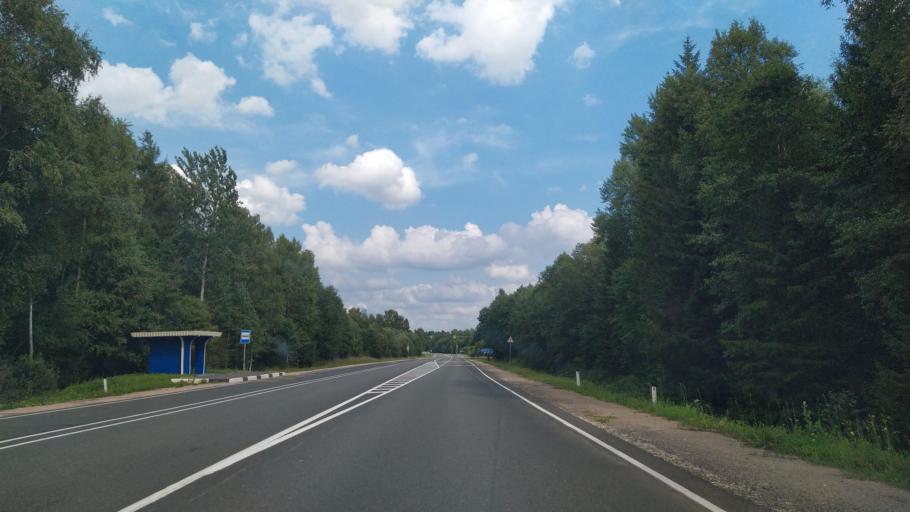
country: RU
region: Pskov
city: Dno
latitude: 57.9930
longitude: 29.8427
